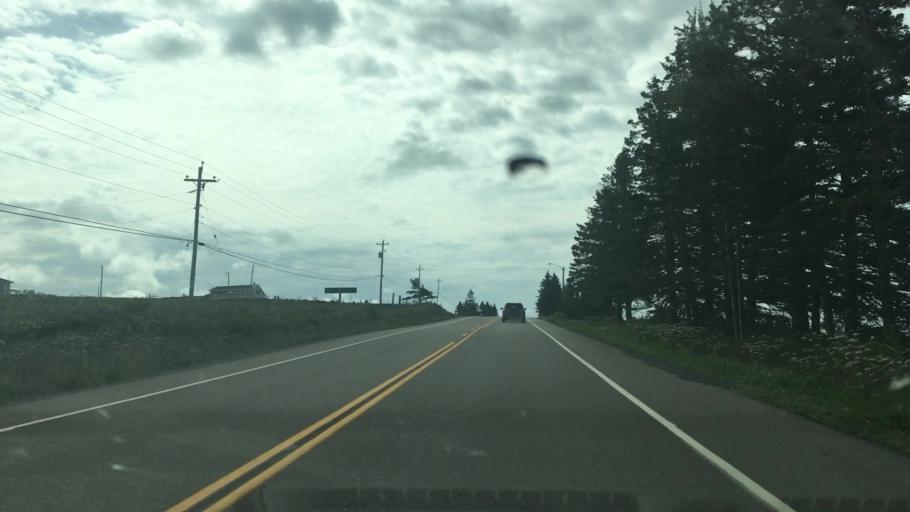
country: CA
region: Nova Scotia
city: Princeville
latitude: 45.6990
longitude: -60.7367
